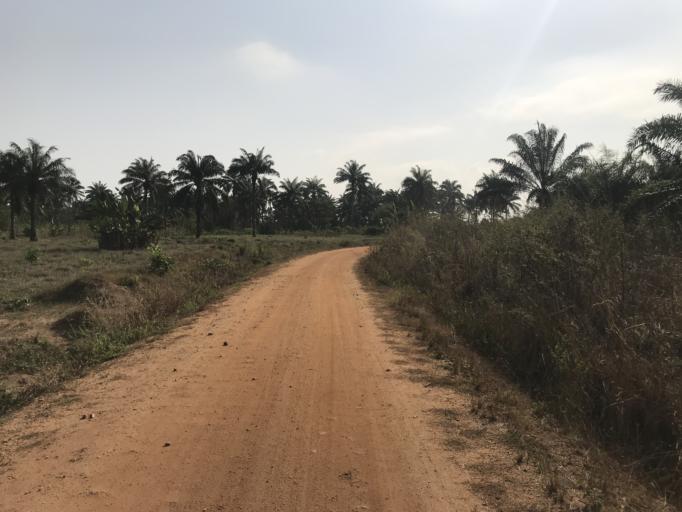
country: NG
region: Osun
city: Olupona
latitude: 7.6115
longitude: 4.1461
